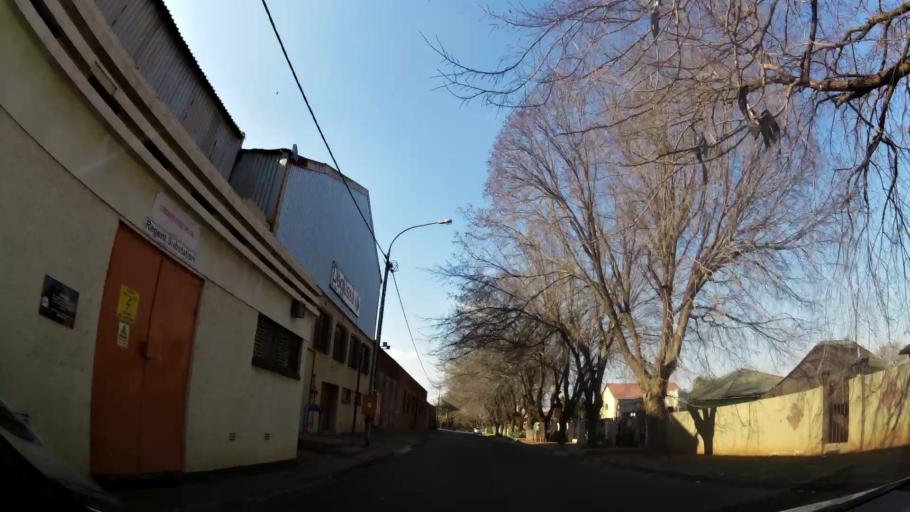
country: ZA
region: Gauteng
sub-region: Ekurhuleni Metropolitan Municipality
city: Brakpan
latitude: -26.2266
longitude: 28.3604
